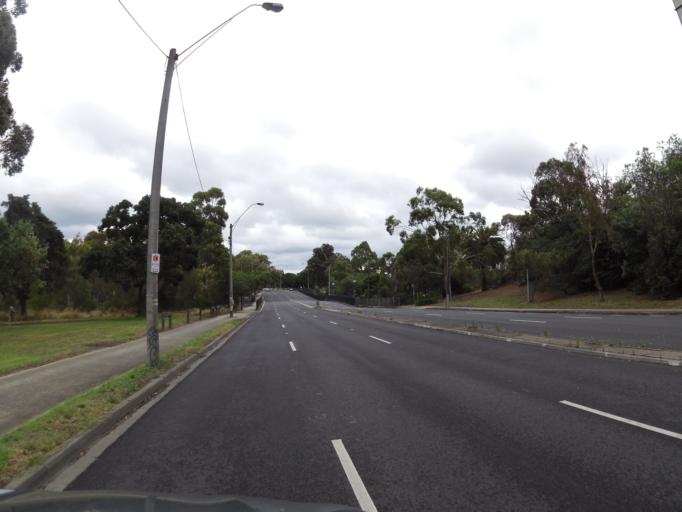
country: AU
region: Victoria
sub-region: Darebin
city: Fairfield
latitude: -37.7841
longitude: 145.0057
